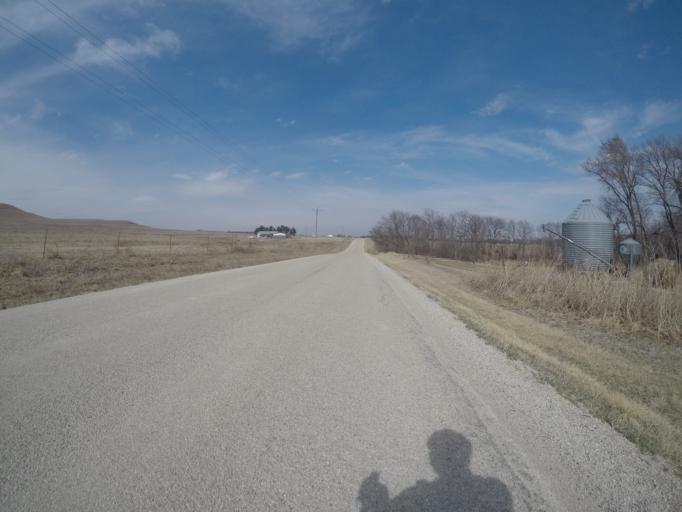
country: US
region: Kansas
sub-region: Geary County
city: Grandview Plaza
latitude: 39.0308
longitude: -96.7430
